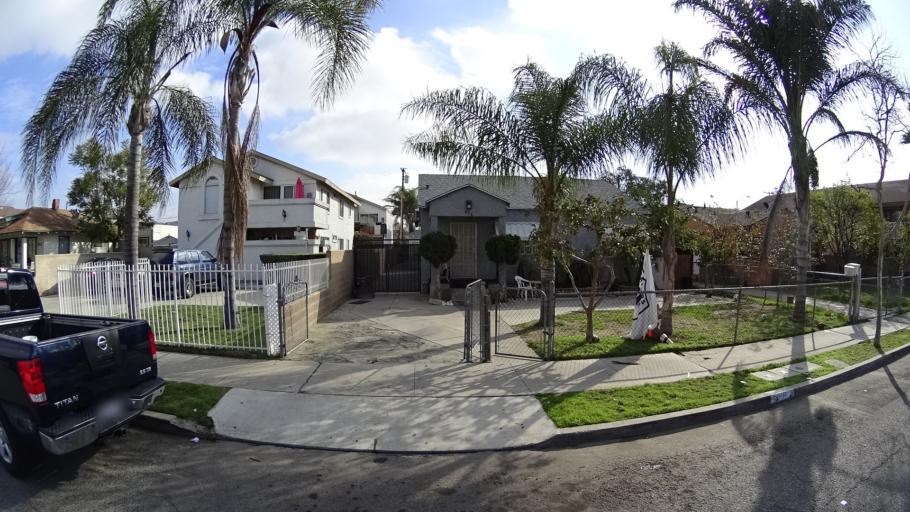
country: US
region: California
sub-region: Orange County
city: Anaheim
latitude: 33.8257
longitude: -117.9093
